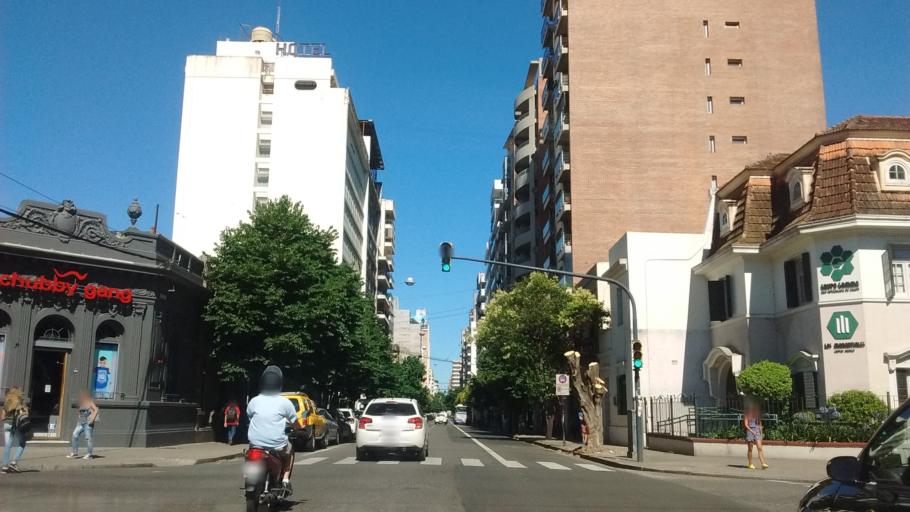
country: AR
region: Santa Fe
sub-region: Departamento de Rosario
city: Rosario
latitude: -32.9427
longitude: -60.6589
